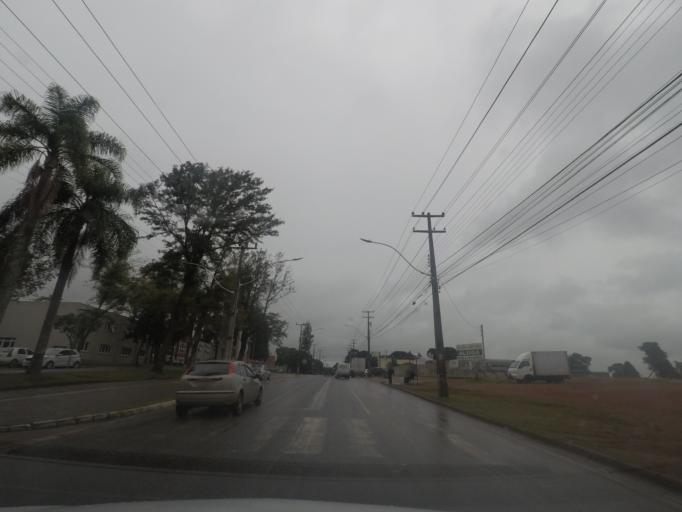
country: BR
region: Parana
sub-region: Piraquara
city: Piraquara
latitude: -25.4505
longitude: -49.0692
